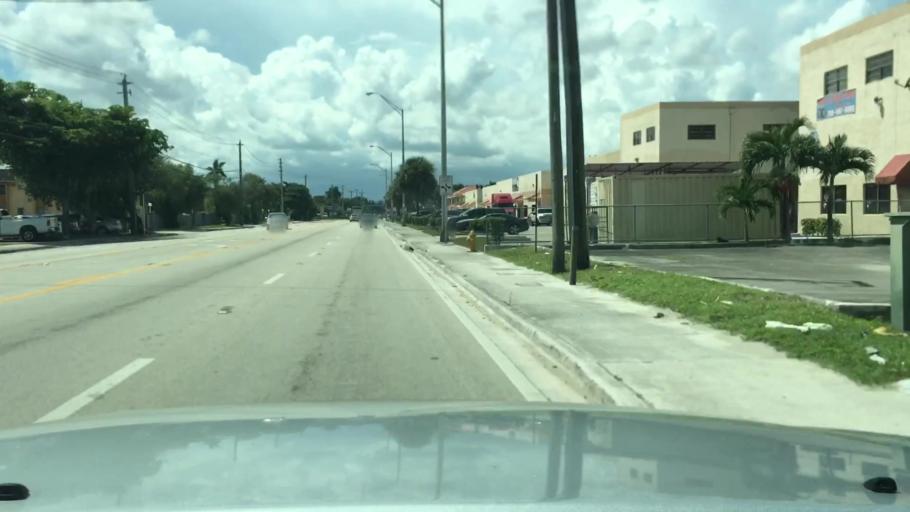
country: US
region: Florida
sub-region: Miami-Dade County
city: Opa-locka
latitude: 25.8966
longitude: -80.2632
